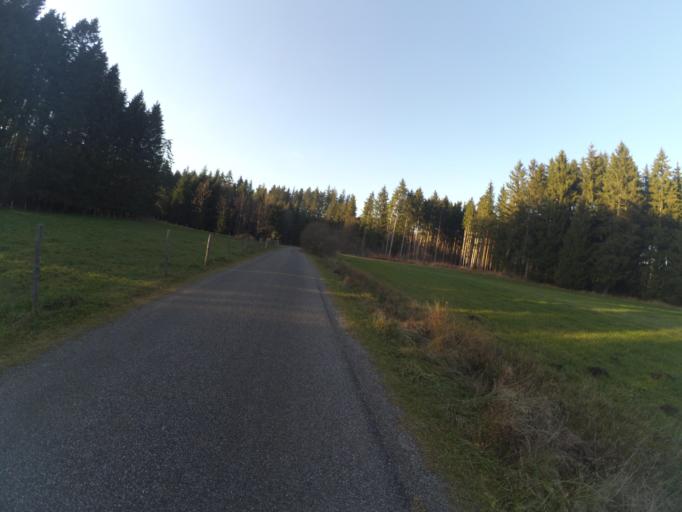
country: DE
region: Bavaria
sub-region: Swabia
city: Aitrang
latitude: 47.7960
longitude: 10.5362
